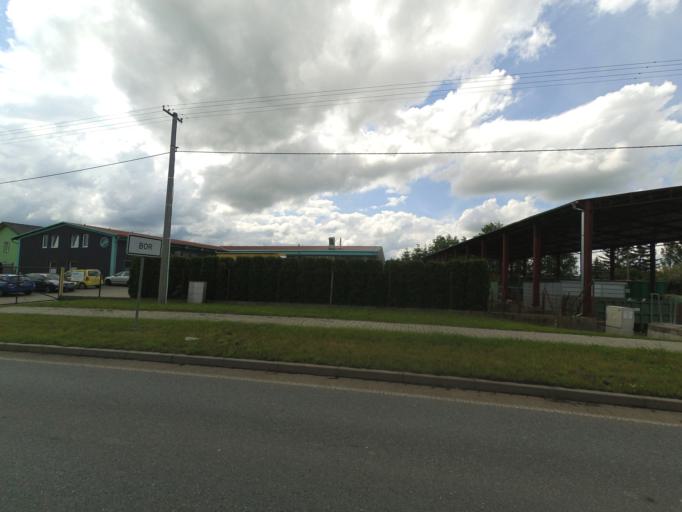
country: CZ
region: Plzensky
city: Bor
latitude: 49.7179
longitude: 12.7780
